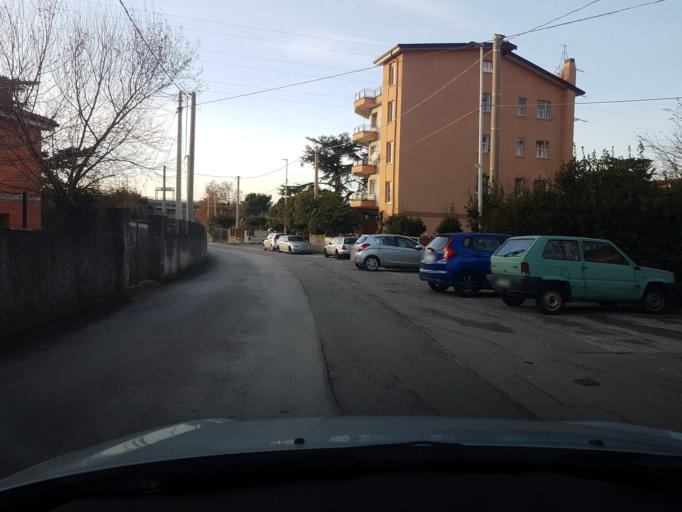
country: IT
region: Friuli Venezia Giulia
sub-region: Provincia di Trieste
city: Domio
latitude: 45.6097
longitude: 13.8317
